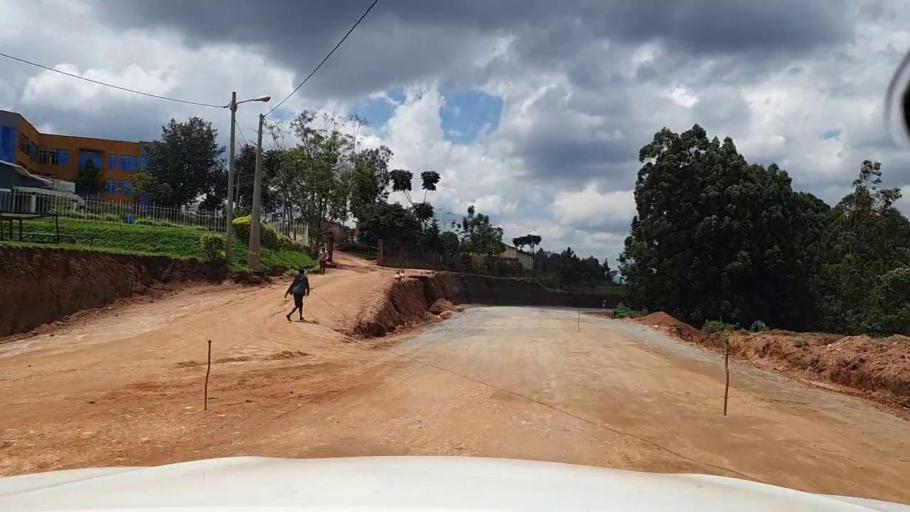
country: RW
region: Southern Province
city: Butare
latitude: -2.6976
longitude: 29.5701
